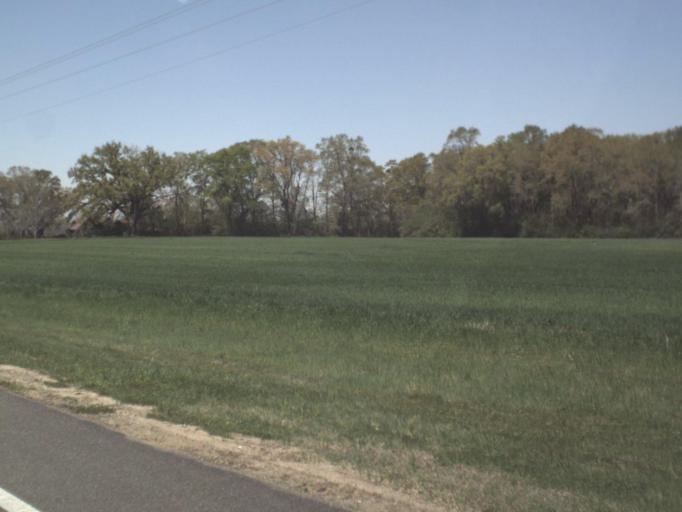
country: US
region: Alabama
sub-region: Geneva County
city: Geneva
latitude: 30.9500
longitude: -85.7385
